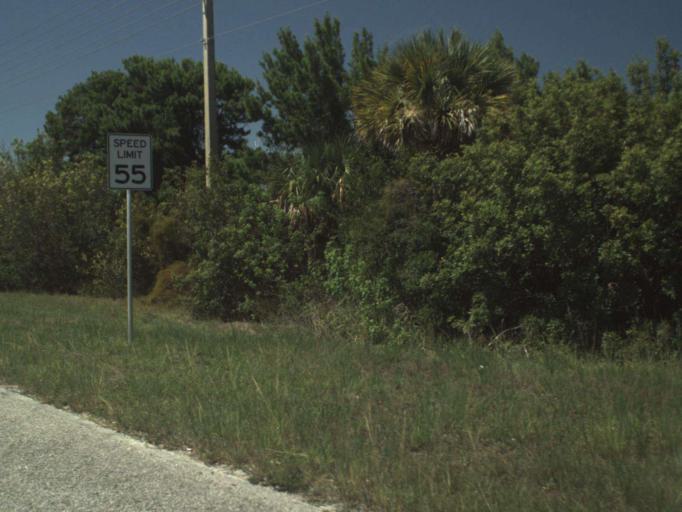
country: US
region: Florida
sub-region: Saint Lucie County
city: Lakewood Park
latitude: 27.5157
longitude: -80.3530
